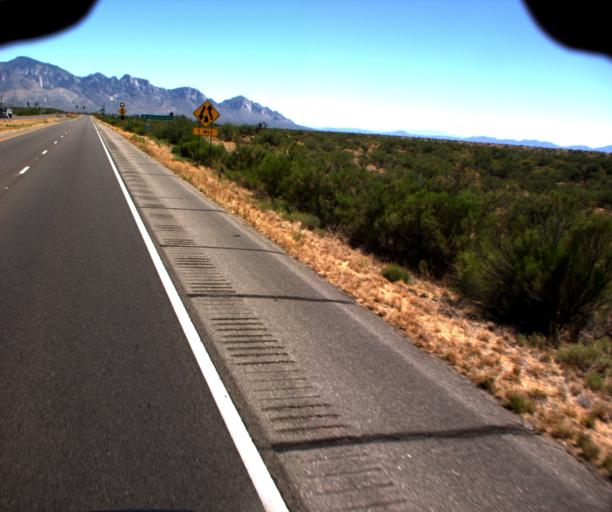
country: US
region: Arizona
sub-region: Pima County
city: Catalina
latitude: 32.5269
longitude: -110.9289
